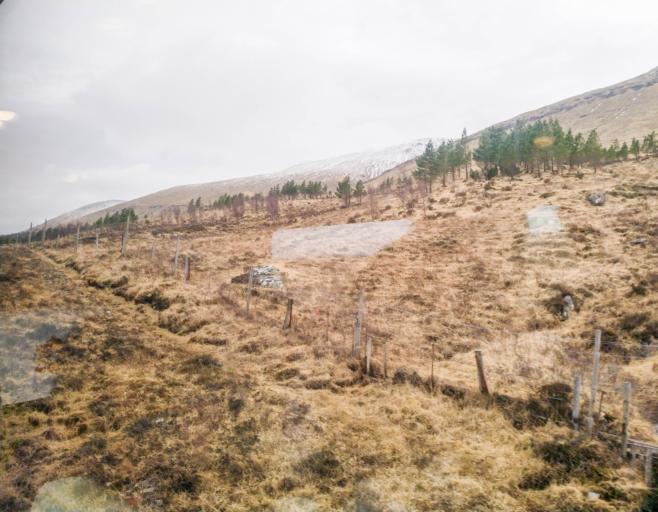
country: GB
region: Scotland
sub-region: Highland
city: Spean Bridge
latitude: 56.5643
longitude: -4.7063
